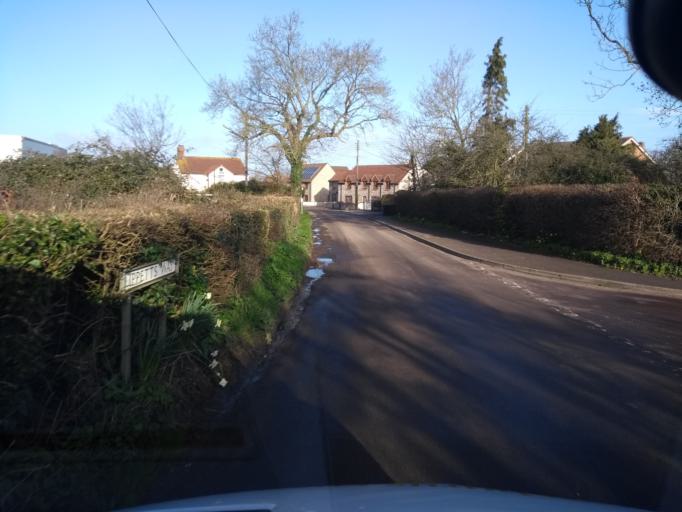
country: GB
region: England
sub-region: Somerset
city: Westonzoyland
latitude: 51.1466
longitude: -2.8646
